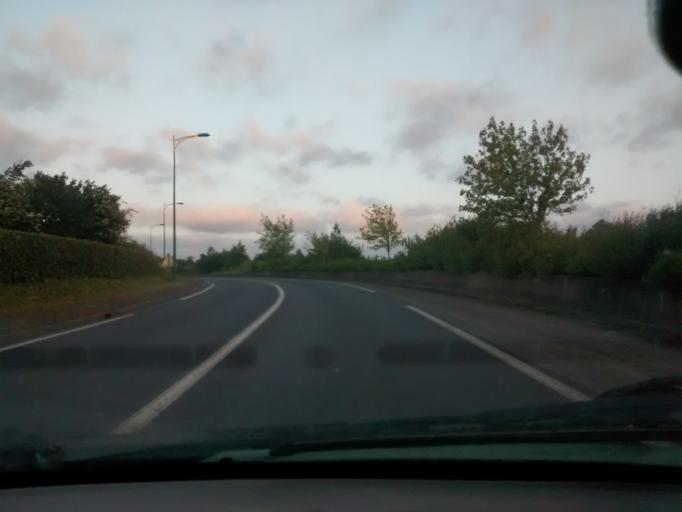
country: FR
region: Lower Normandy
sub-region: Departement de la Manche
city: Agneaux
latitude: 49.1009
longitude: -1.1151
